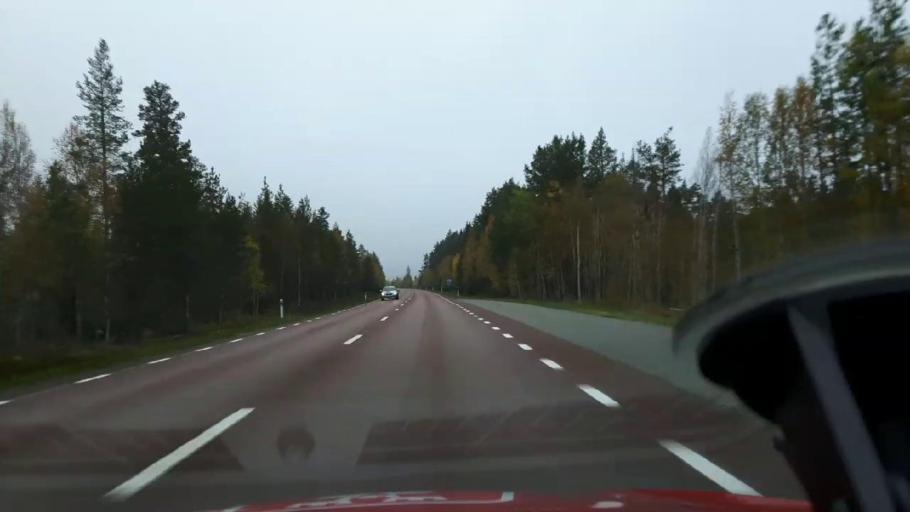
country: SE
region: Jaemtland
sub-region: Bergs Kommun
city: Hoverberg
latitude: 62.5388
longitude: 14.4491
